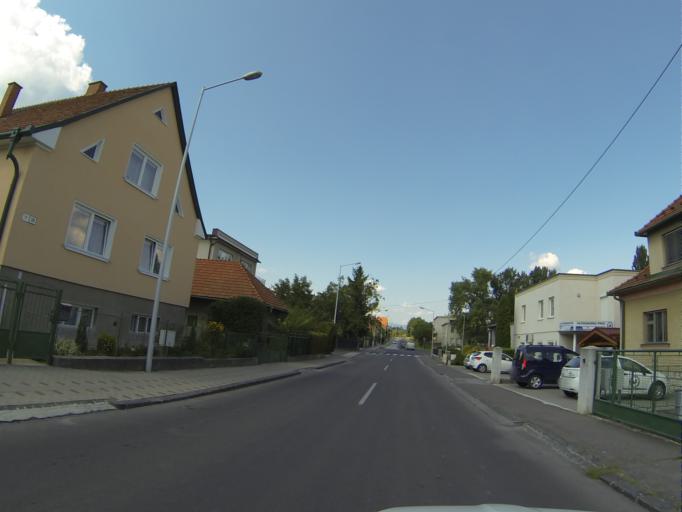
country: SK
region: Nitriansky
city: Bojnice
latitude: 48.7850
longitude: 18.5859
